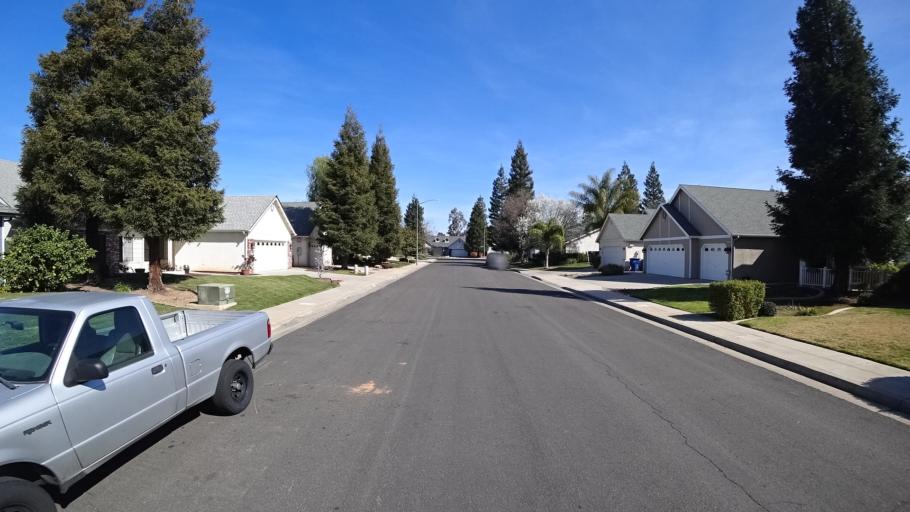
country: US
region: California
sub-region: Fresno County
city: Clovis
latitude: 36.8495
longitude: -119.7369
